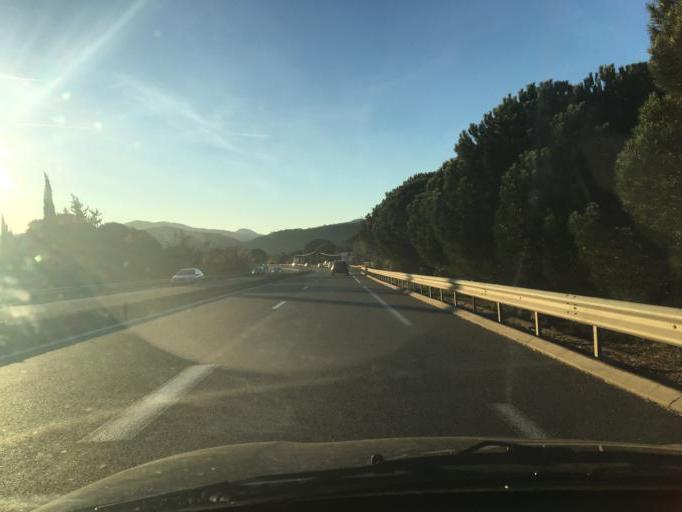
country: FR
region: Provence-Alpes-Cote d'Azur
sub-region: Departement du Var
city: Le Muy
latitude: 43.4656
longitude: 6.5459
